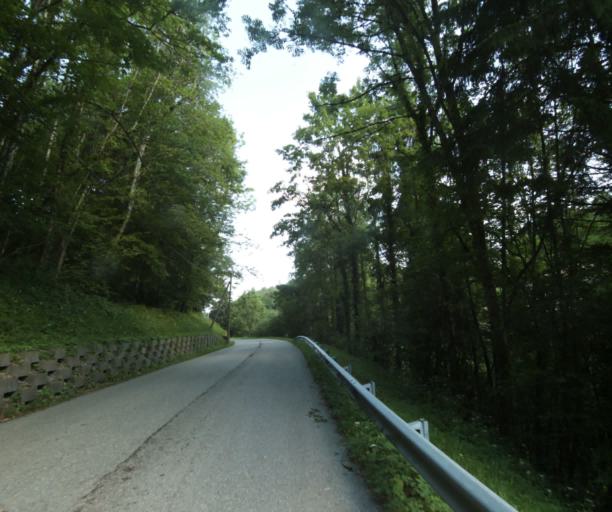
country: FR
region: Rhone-Alpes
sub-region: Departement de la Haute-Savoie
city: Lyaud
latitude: 46.3157
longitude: 6.5064
